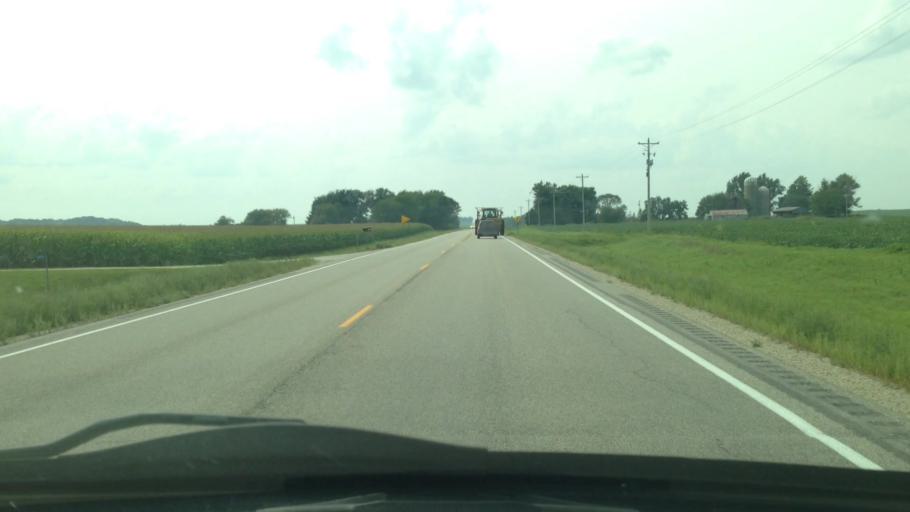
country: US
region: Minnesota
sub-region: Wabasha County
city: Elgin
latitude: 44.1655
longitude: -92.2847
